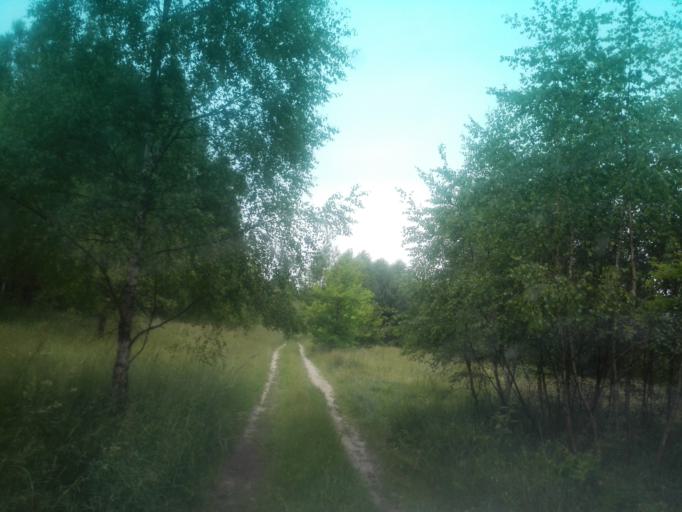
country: PL
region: Silesian Voivodeship
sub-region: Powiat czestochowski
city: Olsztyn
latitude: 50.7870
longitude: 19.2720
